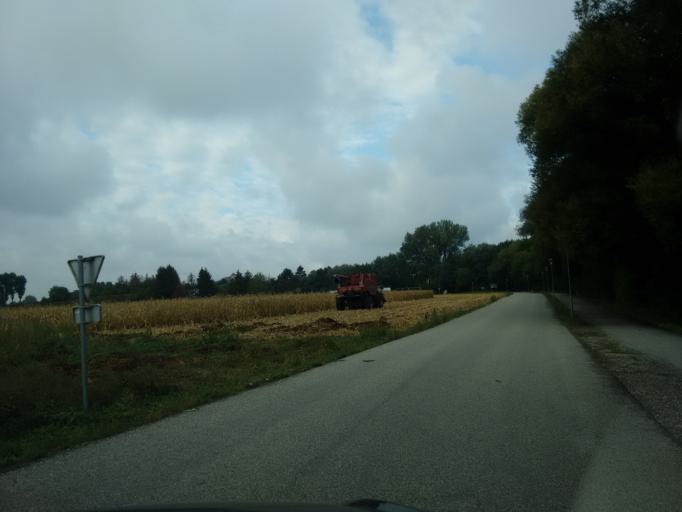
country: AT
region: Upper Austria
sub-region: Wels-Land
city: Marchtrenk
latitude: 48.1871
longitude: 14.1180
